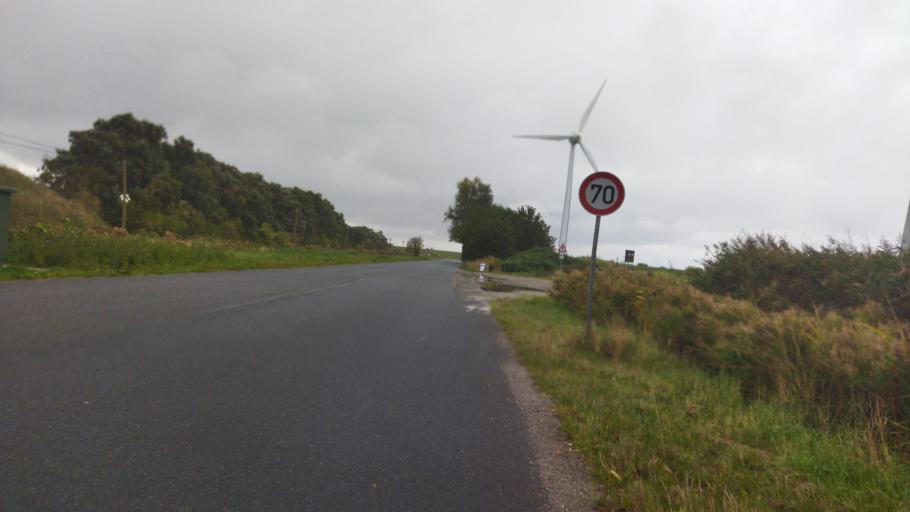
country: DE
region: Lower Saxony
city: Emden
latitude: 53.3396
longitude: 7.1365
